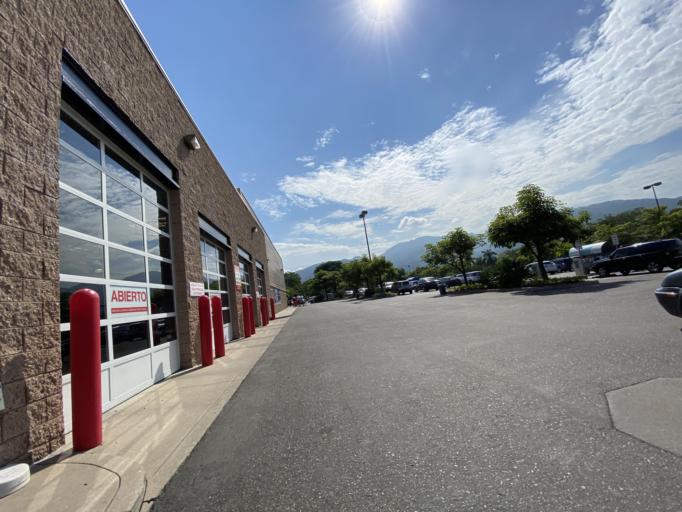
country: MX
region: Jalisco
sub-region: Puerto Vallarta
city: Puerto Vallarta
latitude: 20.6406
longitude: -105.2240
